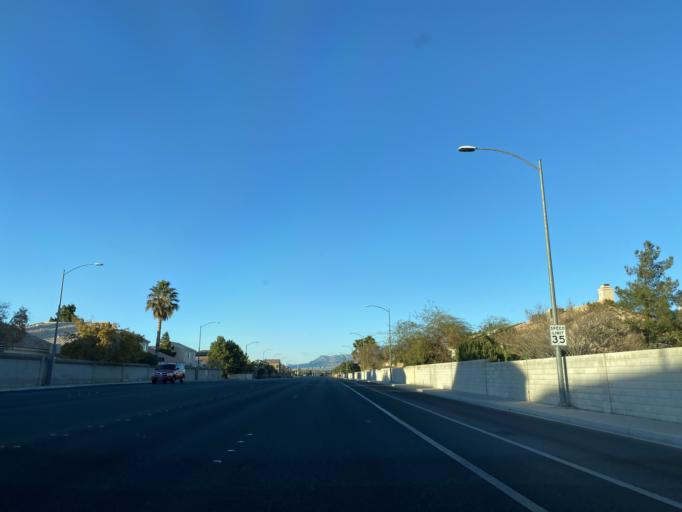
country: US
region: Nevada
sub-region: Clark County
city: Summerlin South
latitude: 36.2265
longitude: -115.2974
